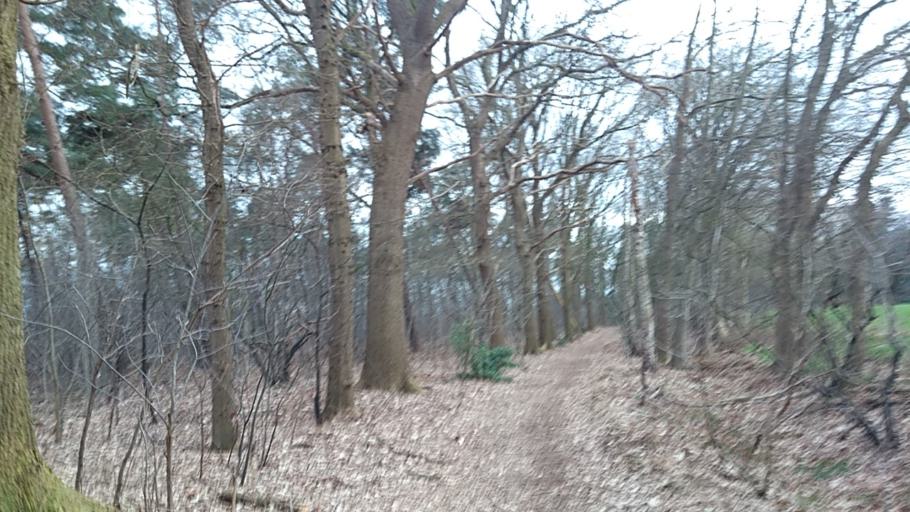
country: NL
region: Overijssel
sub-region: Gemeente Borne
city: Borne
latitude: 52.3520
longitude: 6.7203
